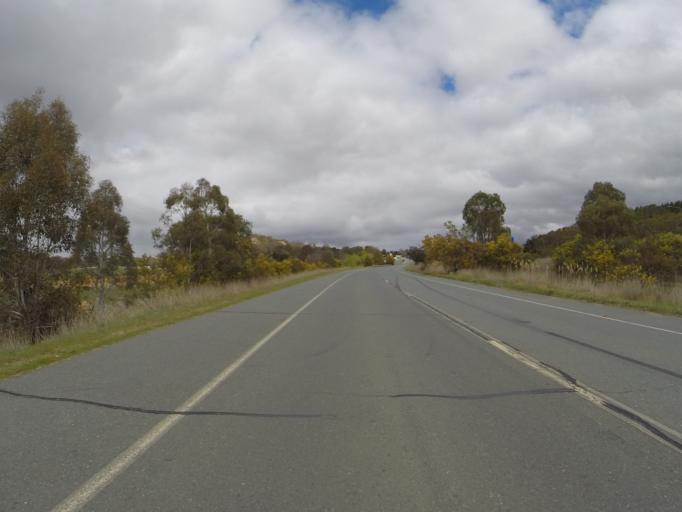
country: AU
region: Australian Capital Territory
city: Kaleen
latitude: -35.1993
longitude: 149.2160
